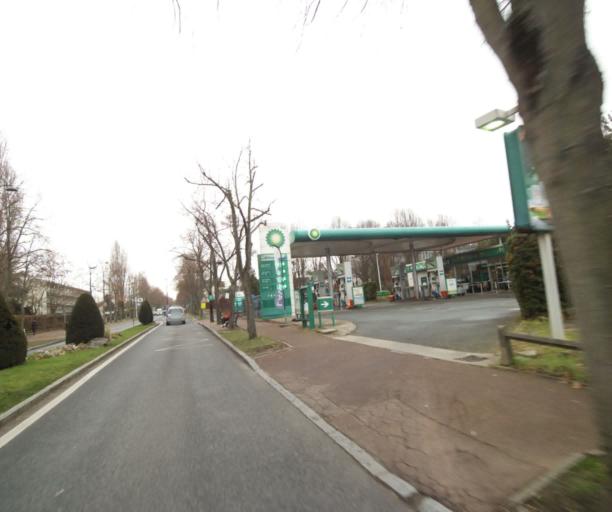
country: FR
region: Ile-de-France
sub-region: Departement des Hauts-de-Seine
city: Rueil-Malmaison
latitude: 48.8620
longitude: 2.1841
